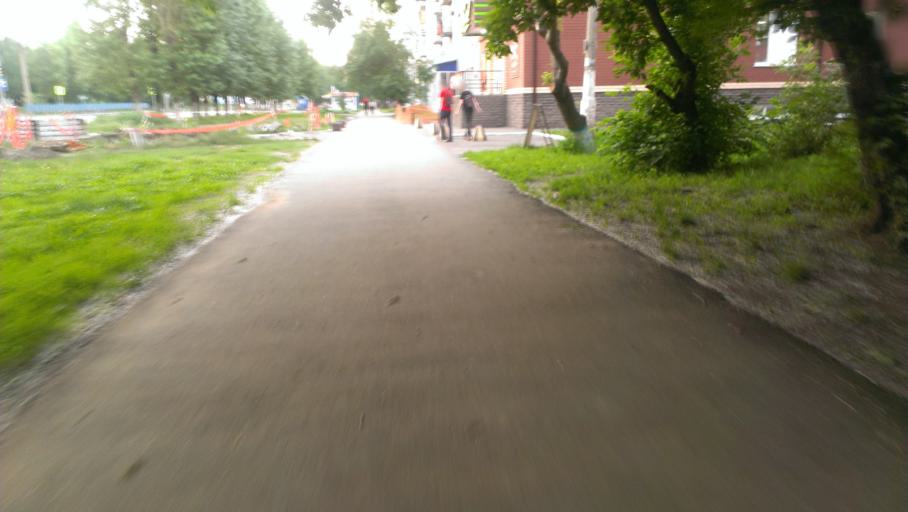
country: RU
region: Altai Krai
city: Novosilikatnyy
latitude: 53.3636
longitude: 83.6763
